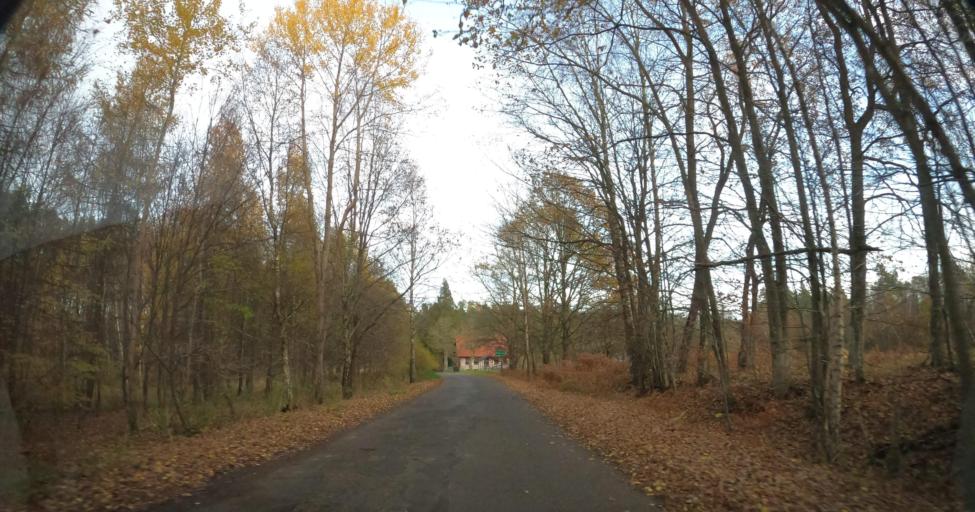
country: PL
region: West Pomeranian Voivodeship
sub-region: Powiat goleniowski
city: Osina
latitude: 53.7057
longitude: 14.9803
